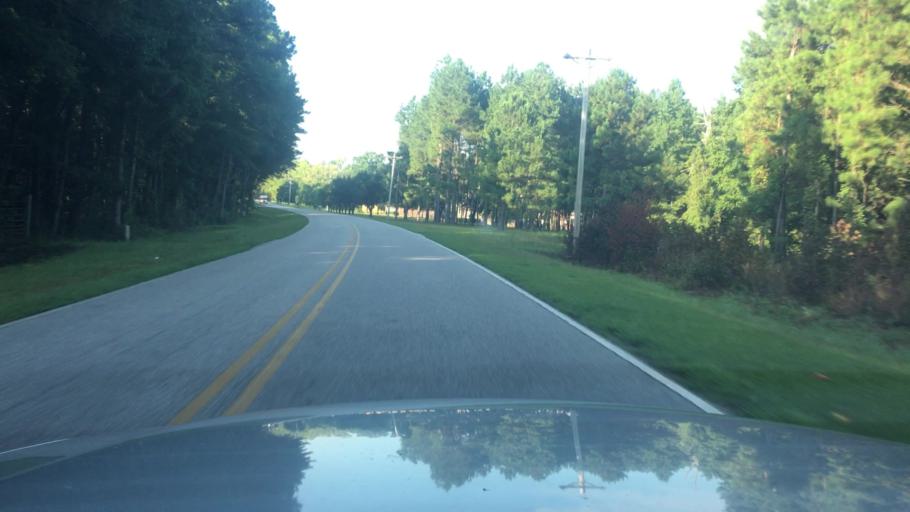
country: US
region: North Carolina
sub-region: Cumberland County
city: Spring Lake
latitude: 35.2236
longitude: -78.8915
